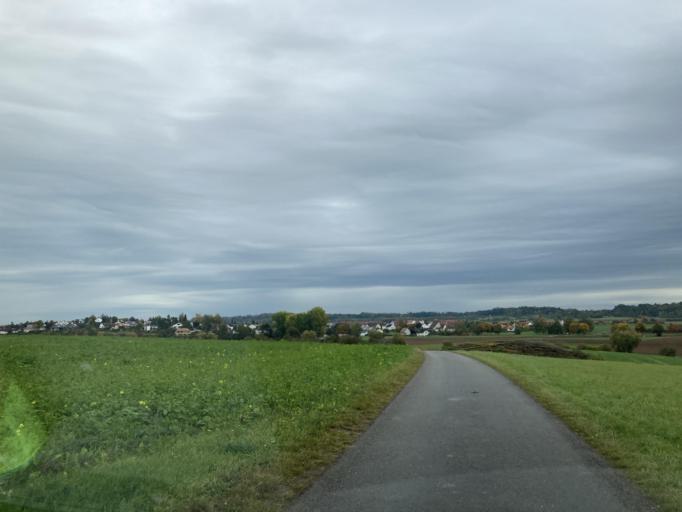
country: DE
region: Baden-Wuerttemberg
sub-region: Regierungsbezirk Stuttgart
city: Bondorf
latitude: 48.5316
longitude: 8.8553
